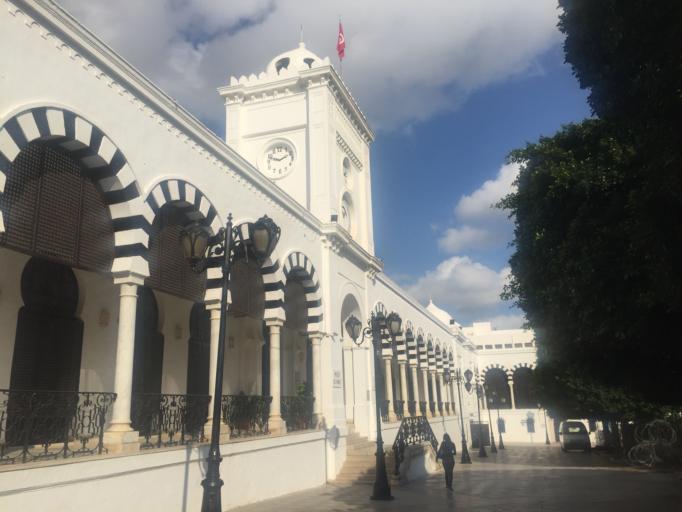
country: TN
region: Tunis
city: Tunis
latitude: 36.7979
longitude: 10.1685
